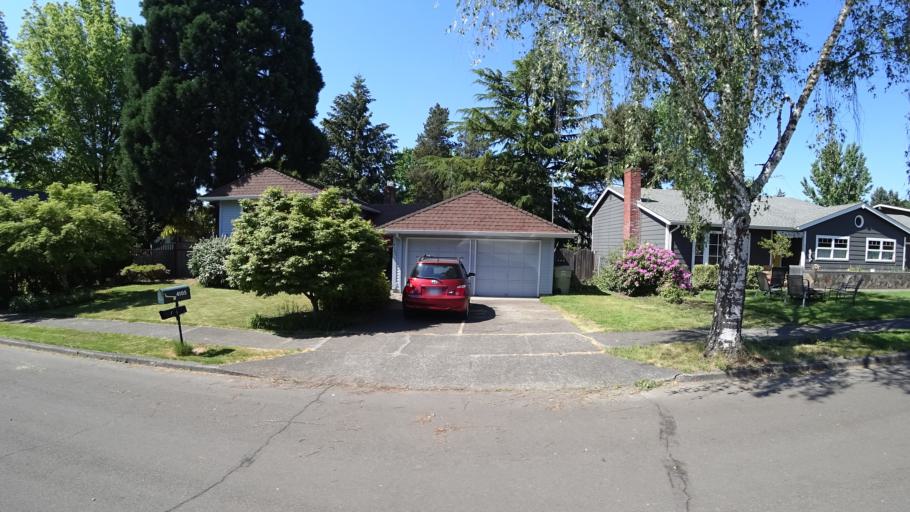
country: US
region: Oregon
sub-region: Washington County
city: Rockcreek
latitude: 45.5484
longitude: -122.8718
